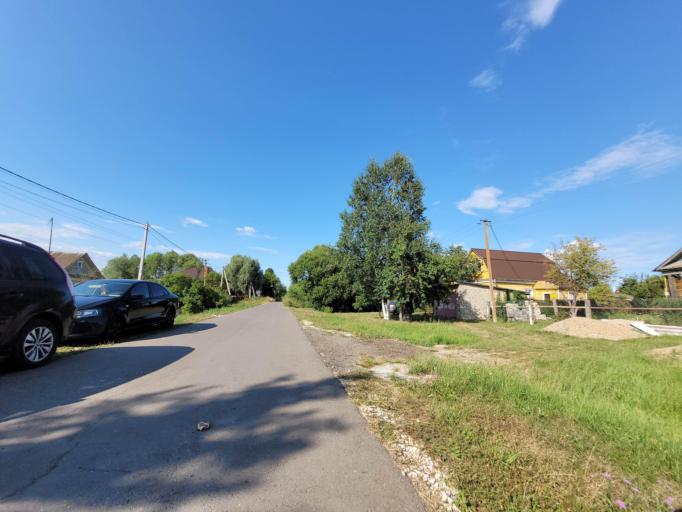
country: RU
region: Moskovskaya
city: Lopatinskiy
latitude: 55.3903
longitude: 38.7143
